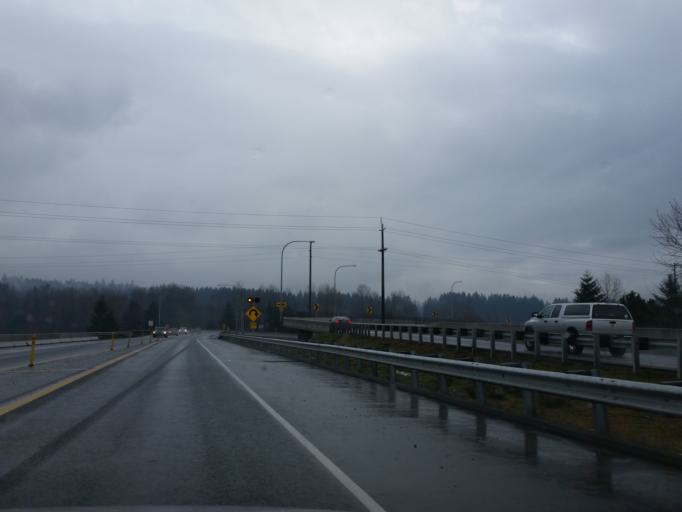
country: US
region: Washington
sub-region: Snohomish County
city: Monroe
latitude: 47.8615
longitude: -121.9851
